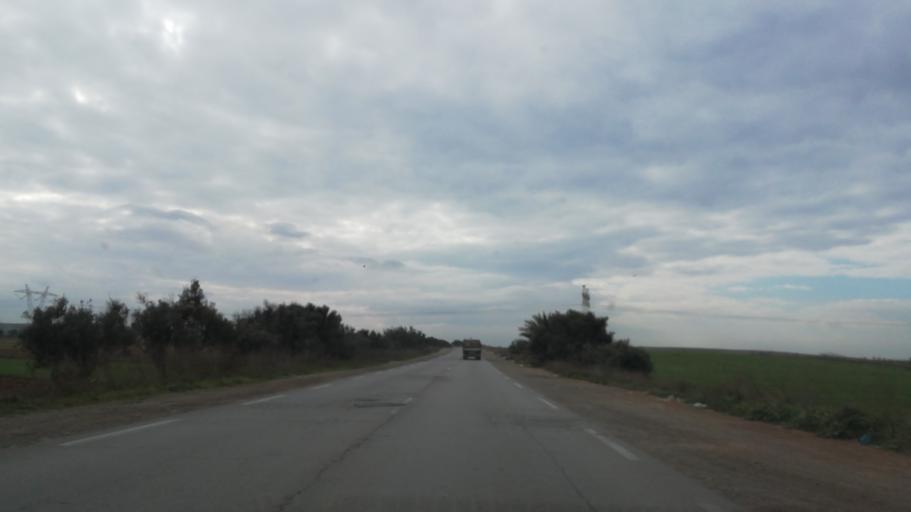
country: DZ
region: Oran
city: Ain el Bya
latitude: 35.7689
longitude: -0.3477
